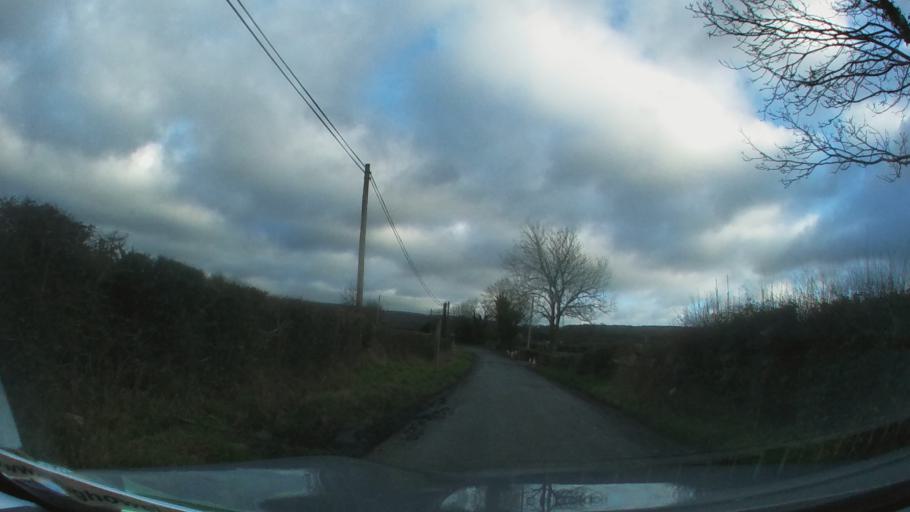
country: IE
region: Leinster
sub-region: Kilkenny
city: Thomastown
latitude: 52.5554
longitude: -7.1116
